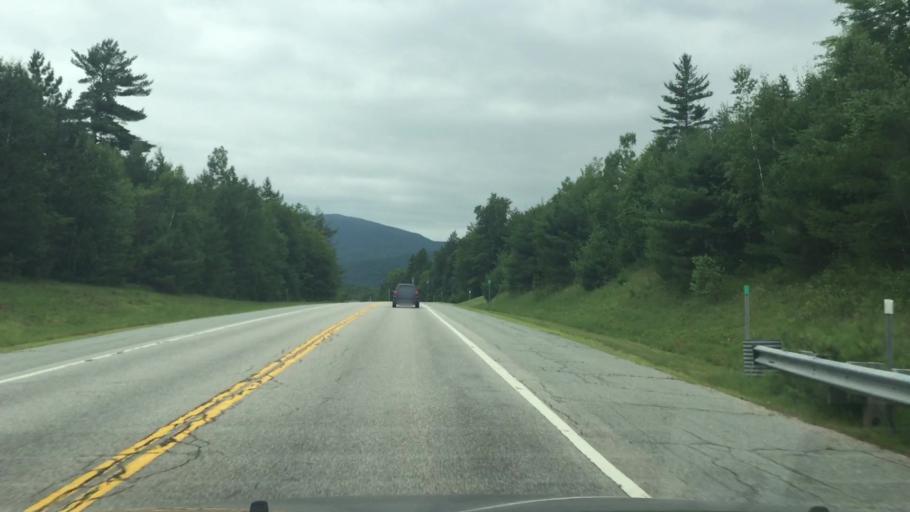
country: US
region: New Hampshire
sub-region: Carroll County
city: North Conway
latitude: 44.1120
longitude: -71.3537
